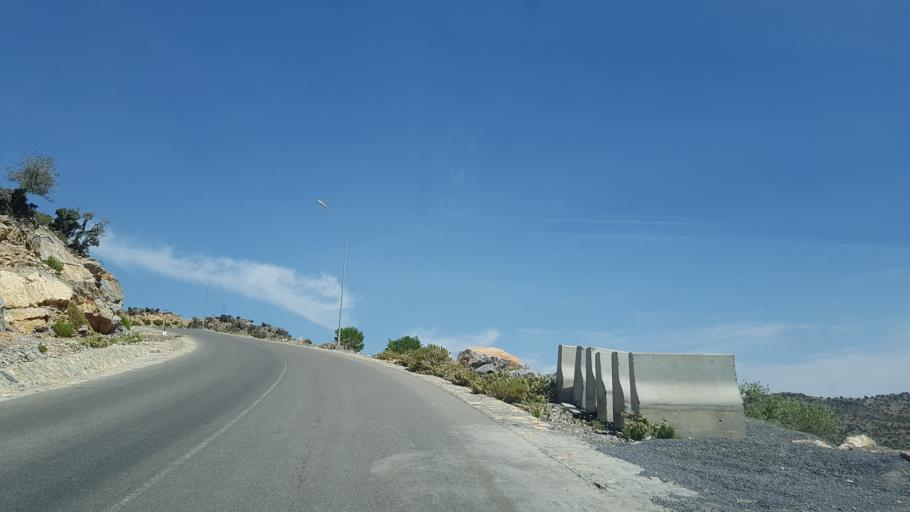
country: OM
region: Al Batinah
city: Bayt al `Awabi
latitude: 23.1353
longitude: 57.5635
